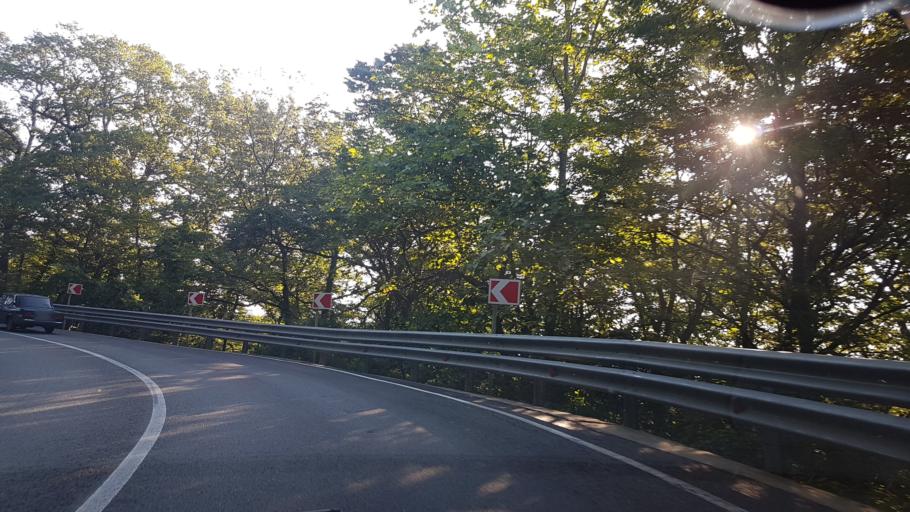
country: RU
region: Krasnodarskiy
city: Dagomys
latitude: 43.6630
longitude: 39.6378
